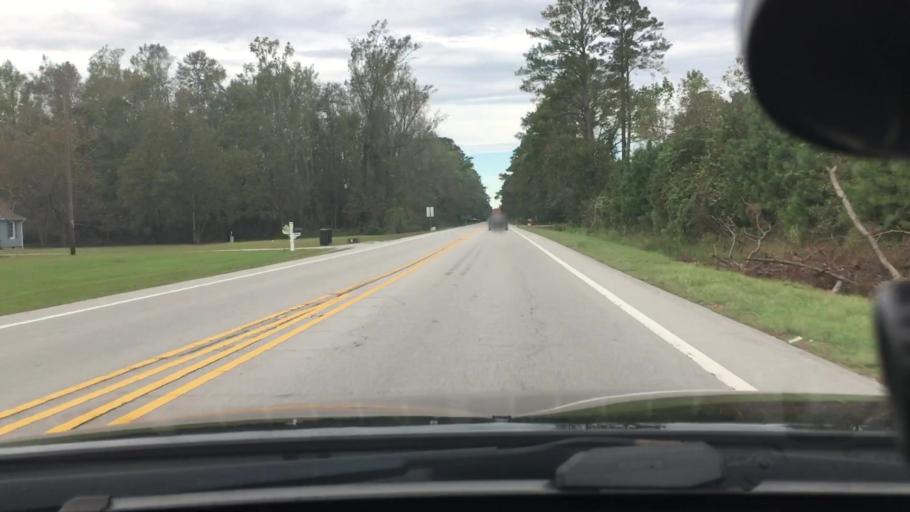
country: US
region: North Carolina
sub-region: Craven County
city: New Bern
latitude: 35.1598
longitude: -77.0380
